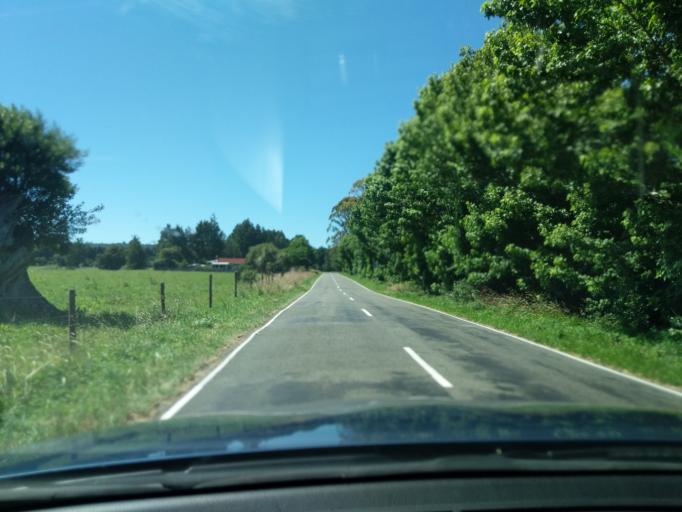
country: NZ
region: Tasman
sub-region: Tasman District
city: Takaka
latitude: -40.7018
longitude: 172.6327
